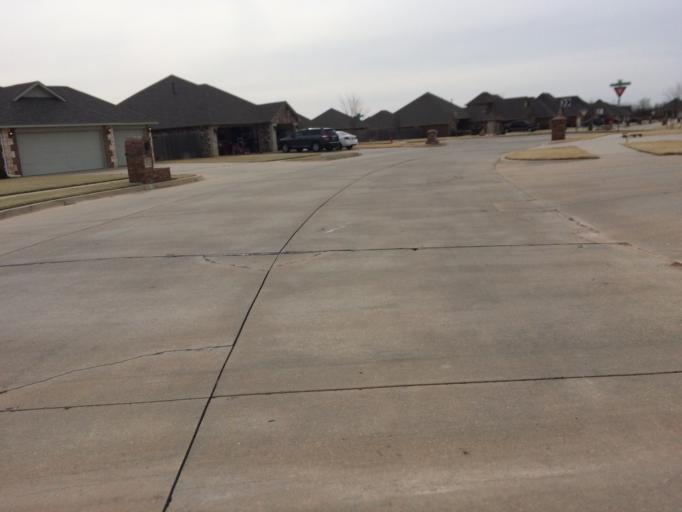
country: US
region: Oklahoma
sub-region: Cleveland County
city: Hall Park
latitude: 35.2139
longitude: -97.3919
